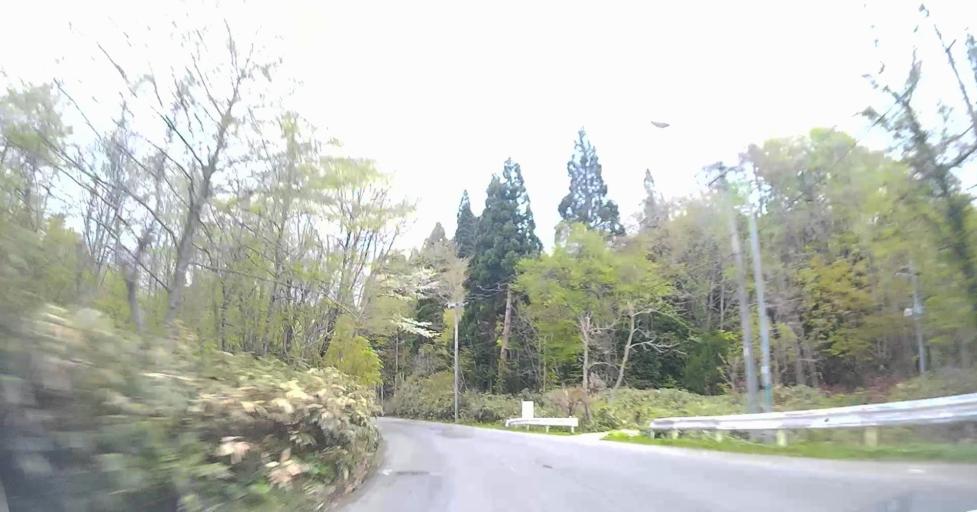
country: JP
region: Aomori
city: Goshogawara
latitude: 41.1137
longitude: 140.5296
